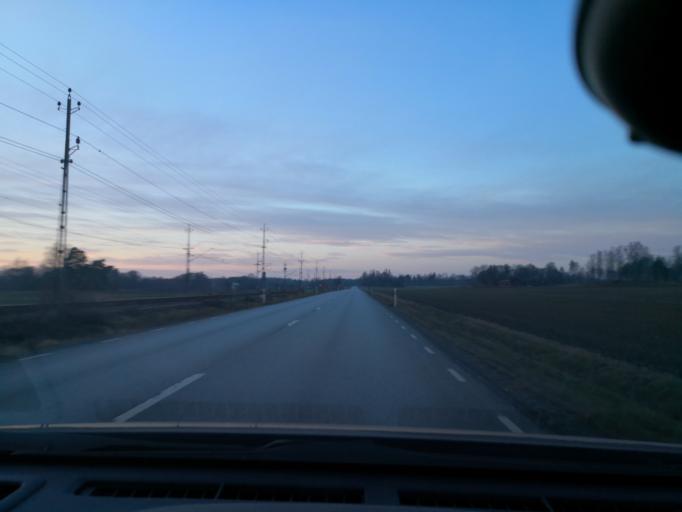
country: SE
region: Vaestmanland
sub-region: Arboga Kommun
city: Arboga
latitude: 59.4059
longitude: 15.8023
